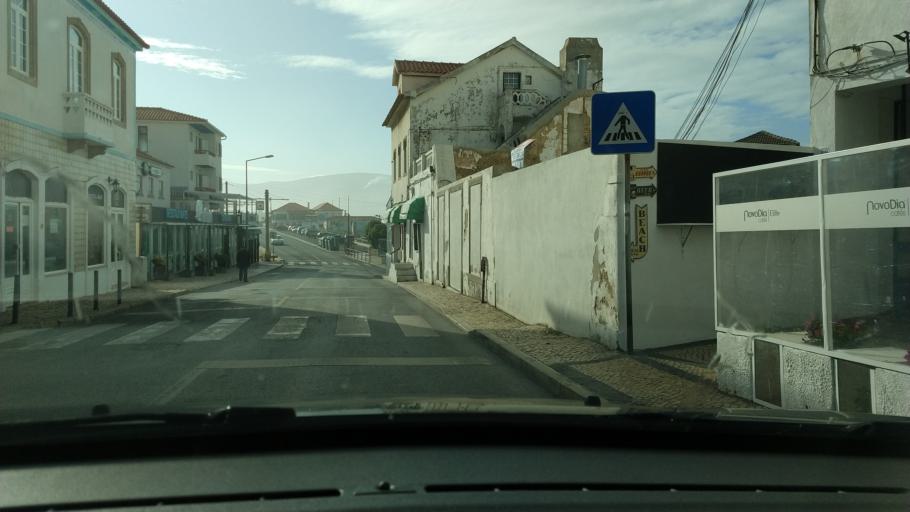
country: PT
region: Lisbon
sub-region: Sintra
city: Colares
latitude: 38.8265
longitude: -9.4691
